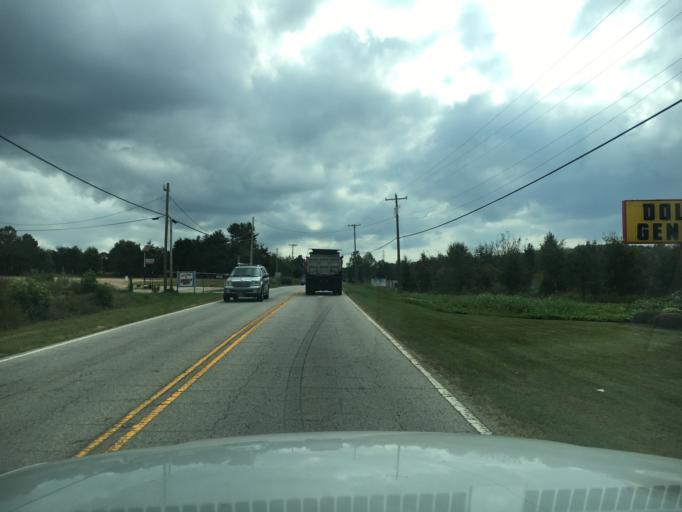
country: US
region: South Carolina
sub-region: Greenville County
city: Greer
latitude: 34.9960
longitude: -82.2479
